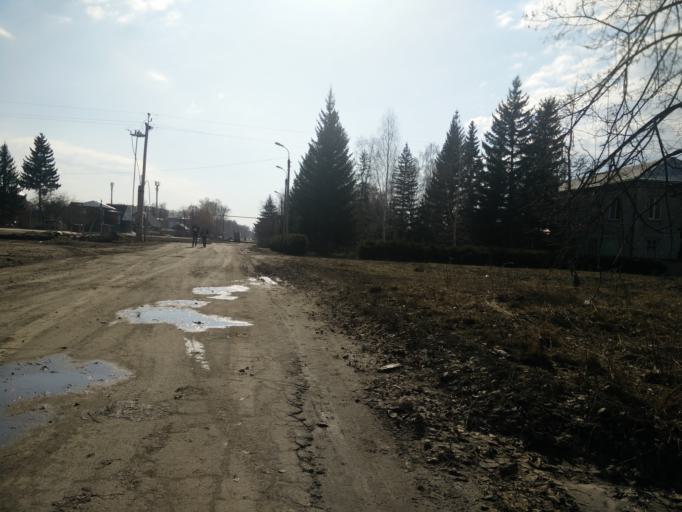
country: RU
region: Novosibirsk
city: Berdsk
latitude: 54.7594
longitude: 83.0676
